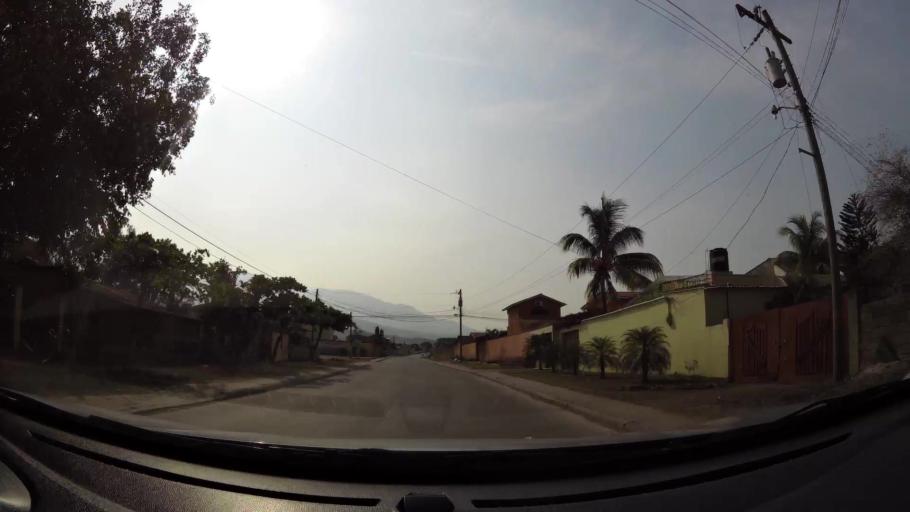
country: HN
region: Comayagua
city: Comayagua
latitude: 14.4534
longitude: -87.6253
